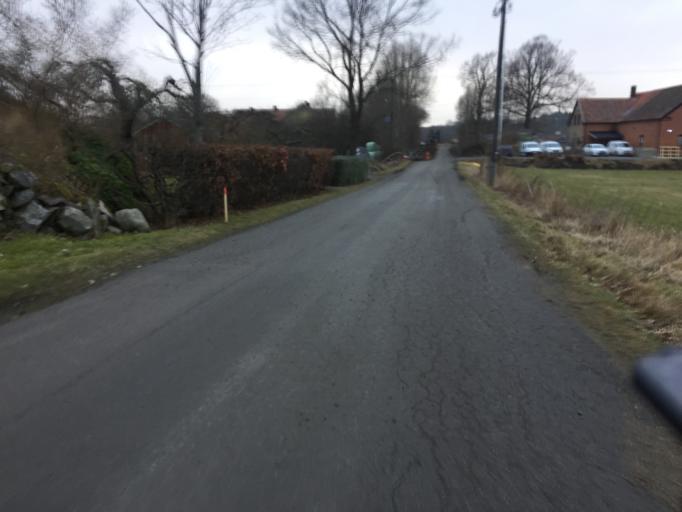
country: SE
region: Blekinge
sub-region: Karlshamns Kommun
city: Morrum
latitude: 56.1759
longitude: 14.7792
